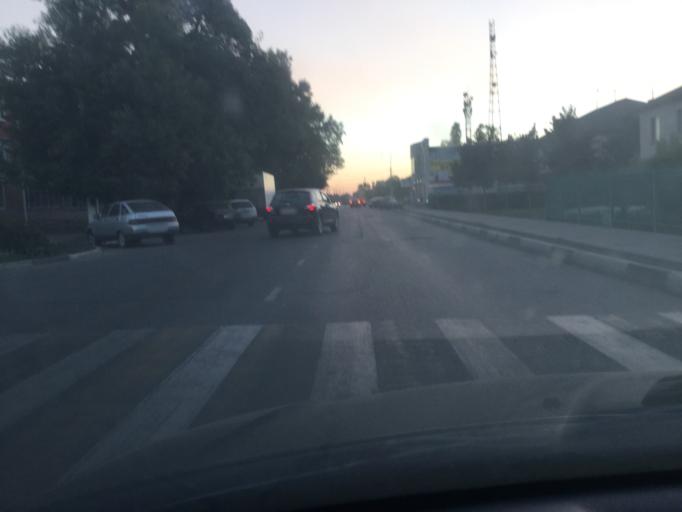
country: RU
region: Krasnodarskiy
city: Slavyansk-na-Kubani
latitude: 45.2533
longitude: 38.1157
